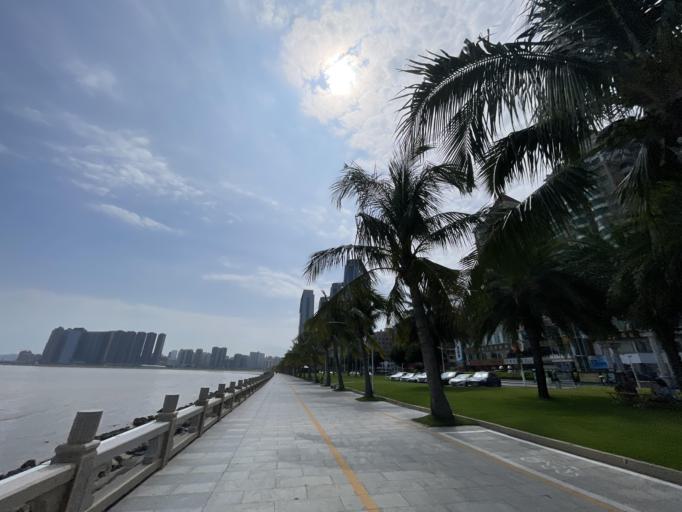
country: MO
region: Macau
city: Macau
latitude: 22.2276
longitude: 113.5578
